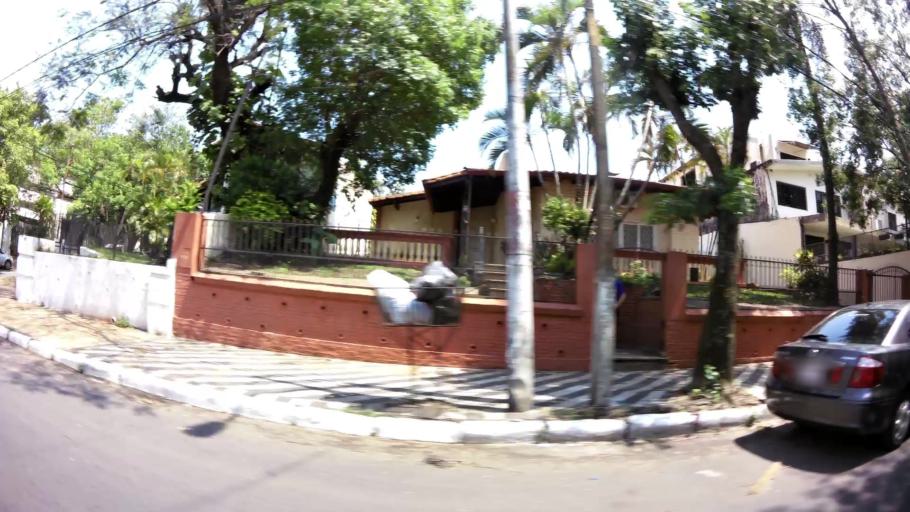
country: PY
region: Asuncion
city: Asuncion
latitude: -25.2942
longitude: -57.6526
